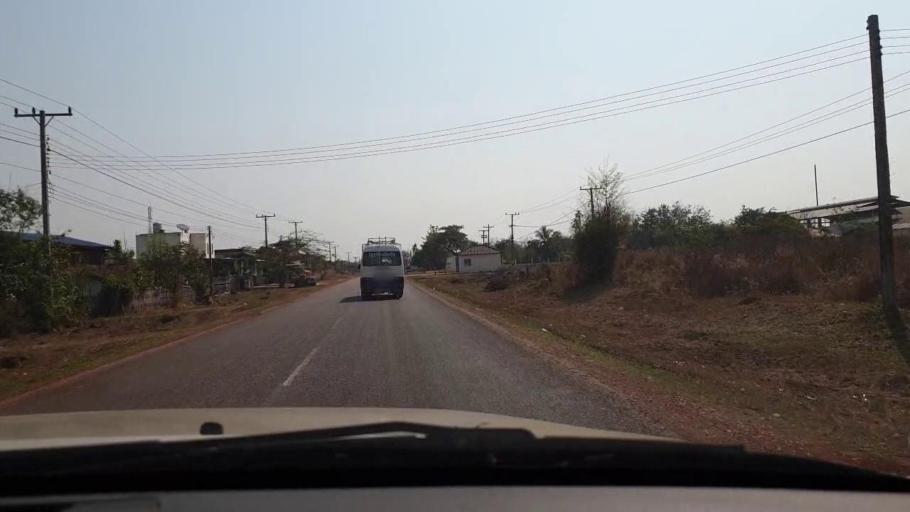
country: TH
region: Nong Khai
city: Nong Khai
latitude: 18.0549
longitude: 102.8334
